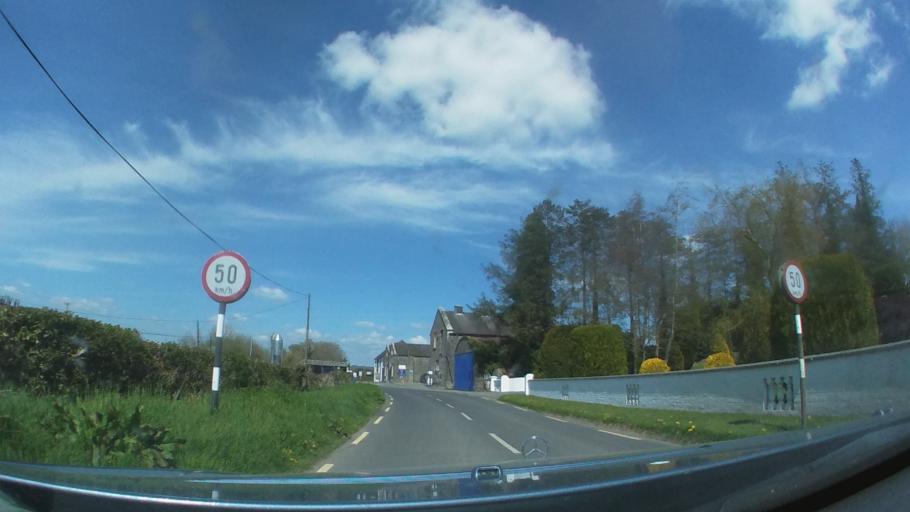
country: IE
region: Leinster
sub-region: Kilkenny
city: Callan
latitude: 52.6199
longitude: -7.4180
